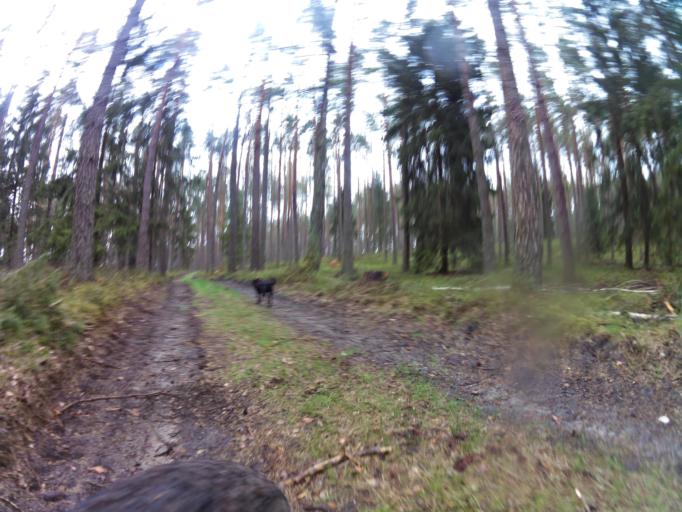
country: PL
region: Pomeranian Voivodeship
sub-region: Powiat slupski
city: Kepice
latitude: 54.2360
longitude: 16.7808
